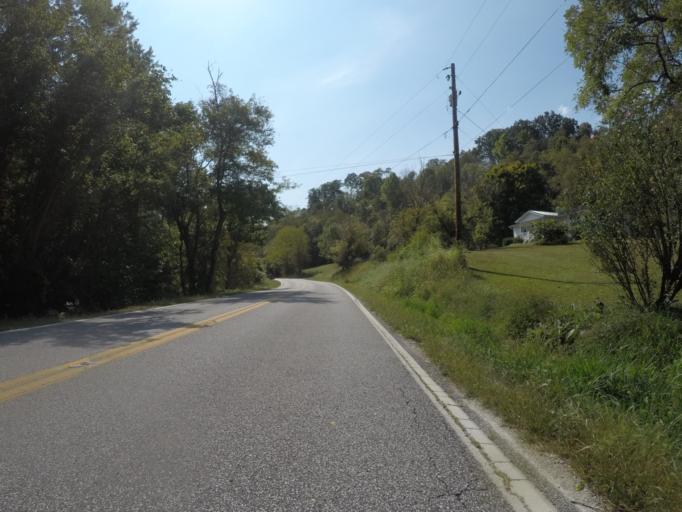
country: US
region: West Virginia
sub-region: Cabell County
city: Lesage
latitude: 38.5323
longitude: -82.3951
